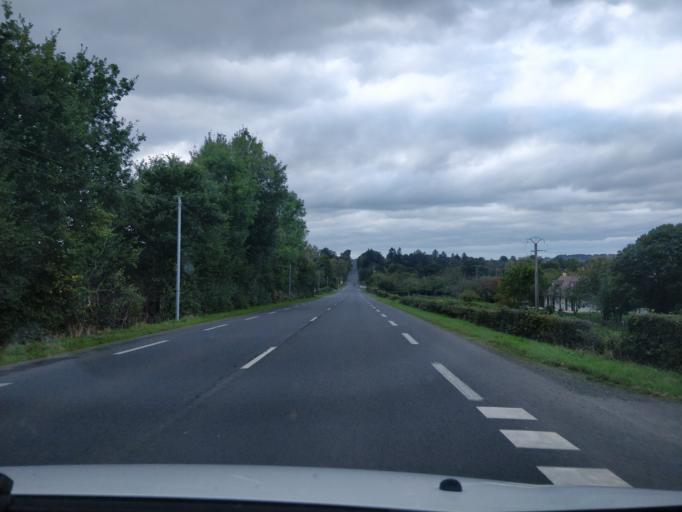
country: FR
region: Lower Normandy
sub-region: Departement de la Manche
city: Villedieu-les-Poeles
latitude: 48.8273
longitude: -1.1519
